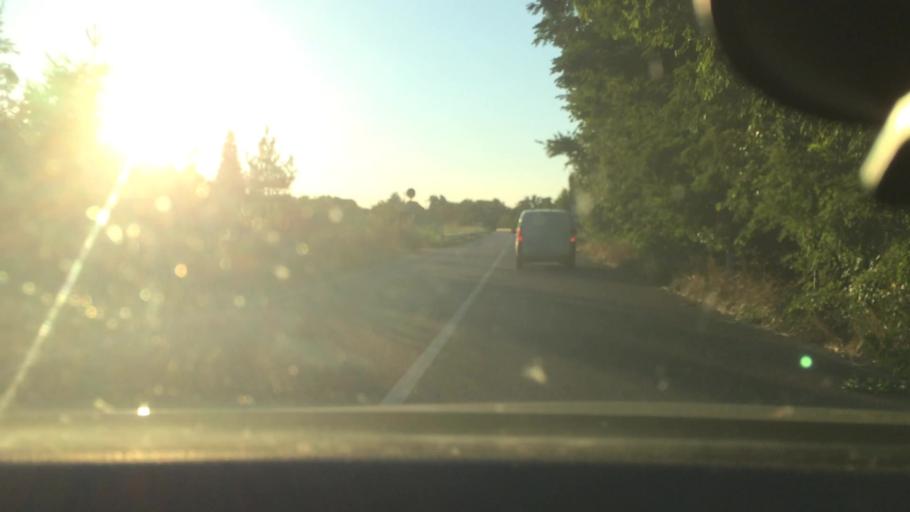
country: IT
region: Lombardy
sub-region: Citta metropolitana di Milano
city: Rescaldina
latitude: 45.6199
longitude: 8.9632
